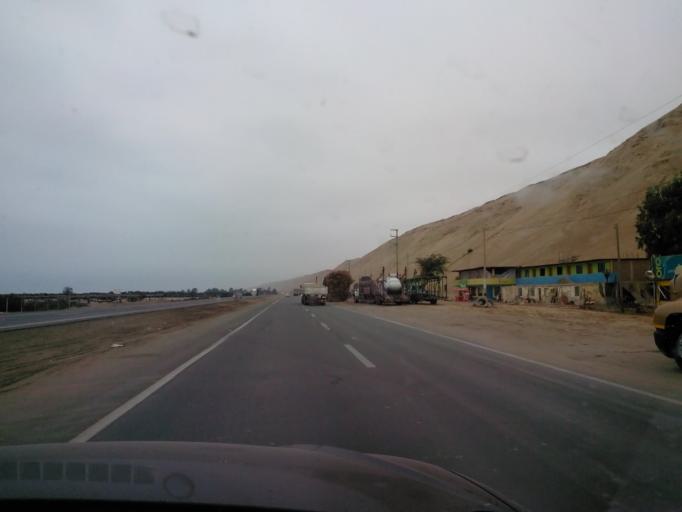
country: PE
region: Ica
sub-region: Provincia de Chincha
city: San Pedro
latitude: -13.3832
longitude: -76.2041
